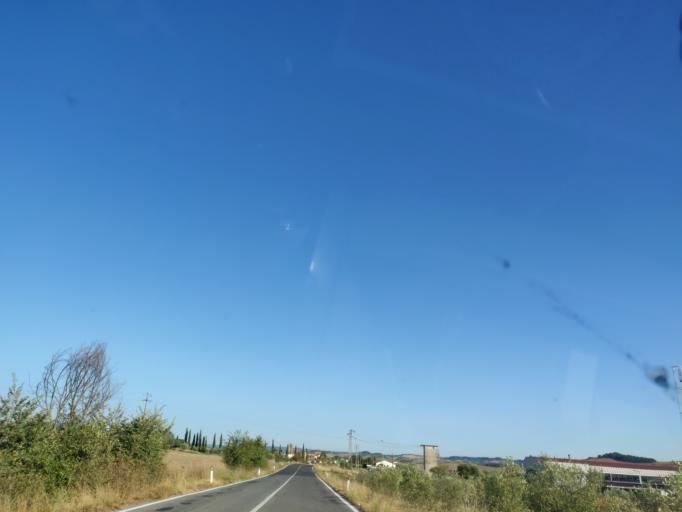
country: IT
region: Tuscany
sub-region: Provincia di Siena
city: Piancastagnaio
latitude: 42.8235
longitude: 11.7276
